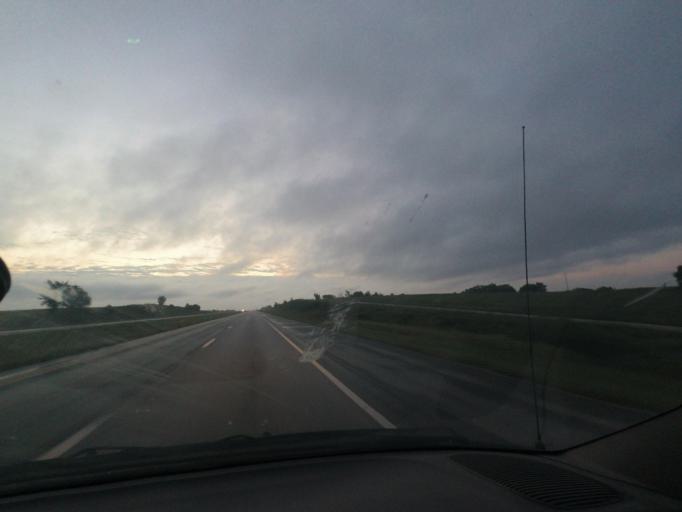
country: US
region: Missouri
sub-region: Linn County
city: Brookfield
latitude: 39.7628
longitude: -93.0199
